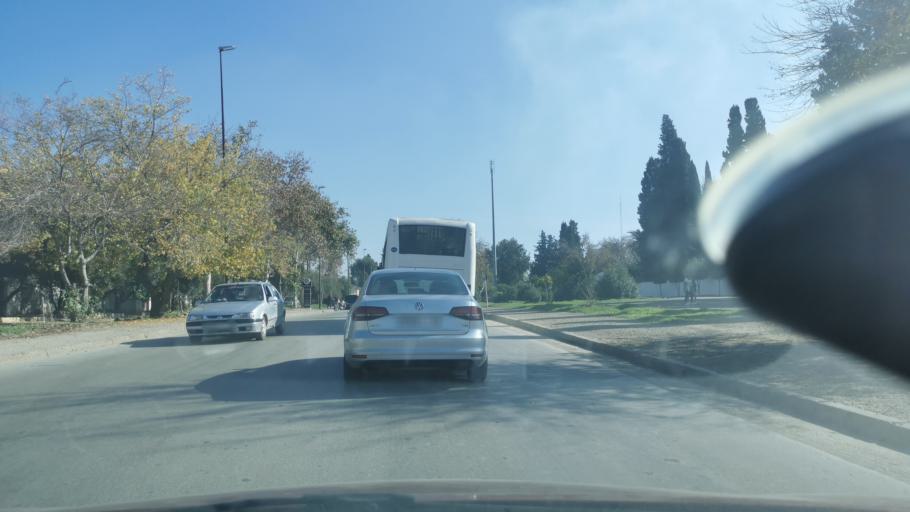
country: MA
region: Fes-Boulemane
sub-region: Fes
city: Fes
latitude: 34.0320
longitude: -4.9872
